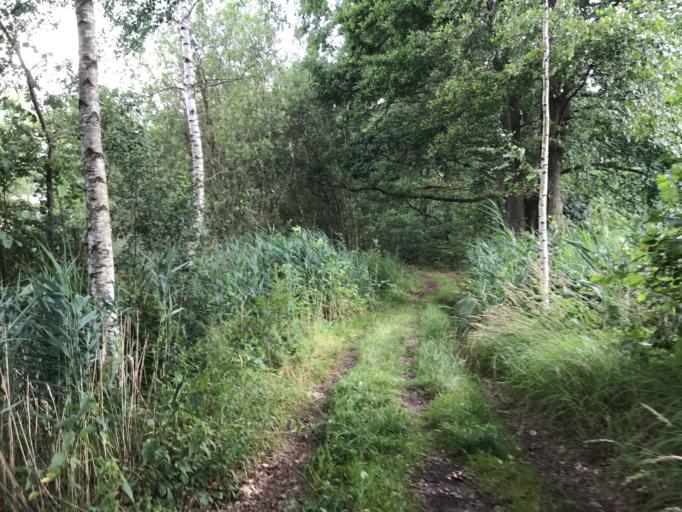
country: CZ
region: Jihocesky
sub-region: Okres Jindrichuv Hradec
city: Lomnice nad Luznici
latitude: 49.0923
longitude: 14.7092
